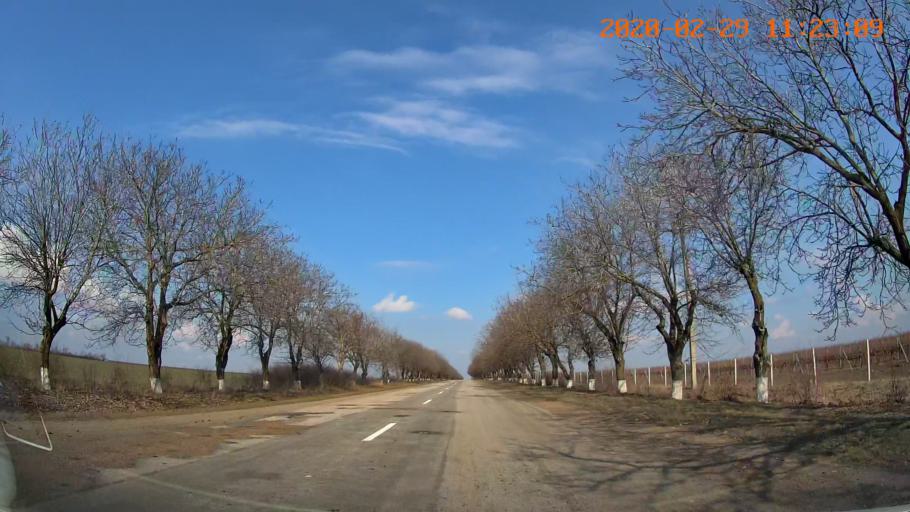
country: MD
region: Telenesti
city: Cocieri
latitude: 47.4039
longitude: 29.1600
